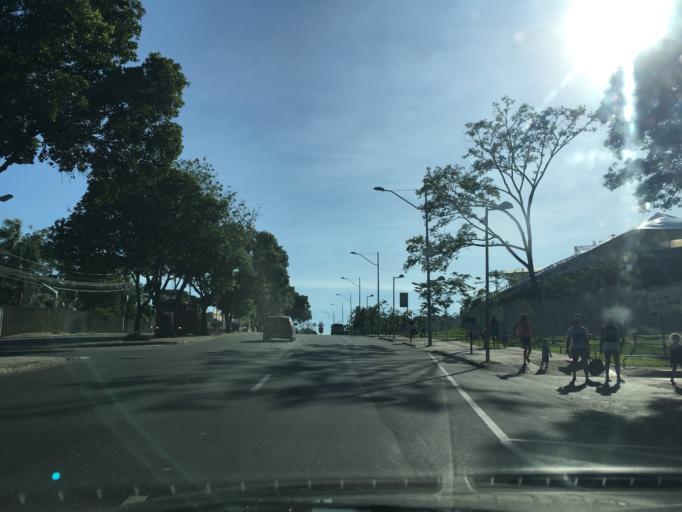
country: BR
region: Minas Gerais
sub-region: Belo Horizonte
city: Belo Horizonte
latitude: -19.8638
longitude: -43.9724
